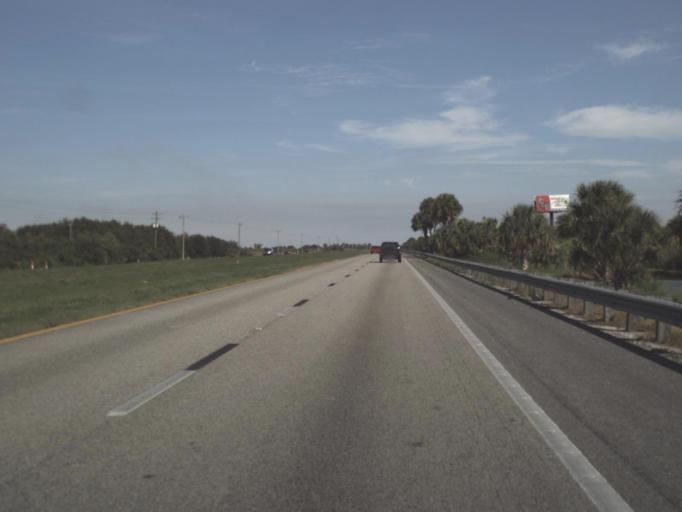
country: US
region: Florida
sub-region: Hendry County
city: Harlem
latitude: 26.7537
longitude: -81.0411
